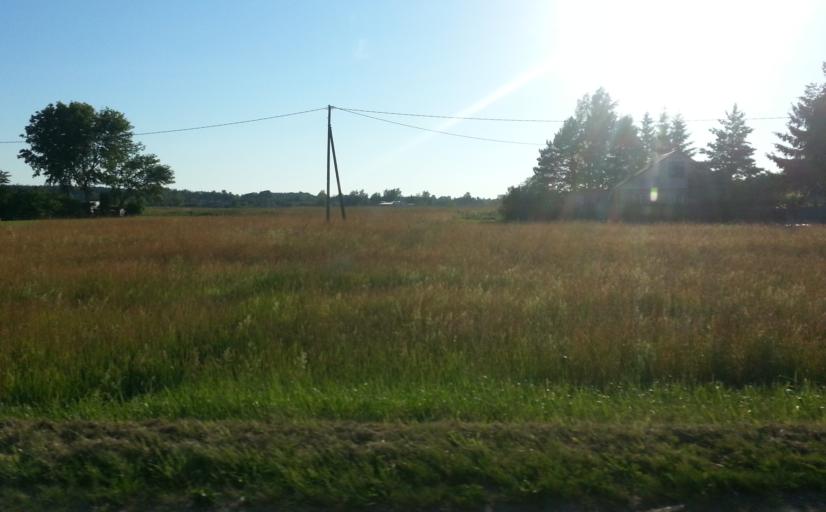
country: LT
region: Panevezys
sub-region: Panevezys City
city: Panevezys
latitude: 55.7930
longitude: 24.3694
